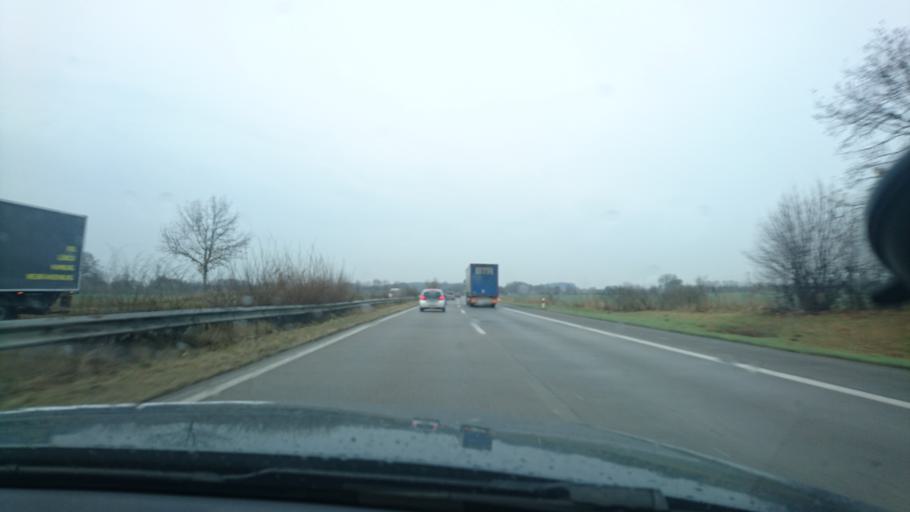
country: DE
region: Schleswig-Holstein
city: Ratekau
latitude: 53.9697
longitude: 10.7343
